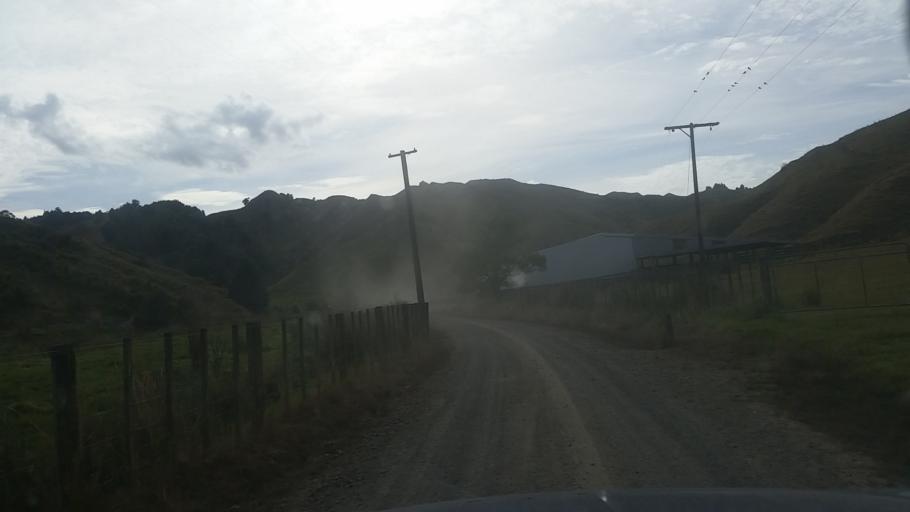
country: NZ
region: Taranaki
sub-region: New Plymouth District
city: Waitara
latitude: -39.1283
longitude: 174.6934
